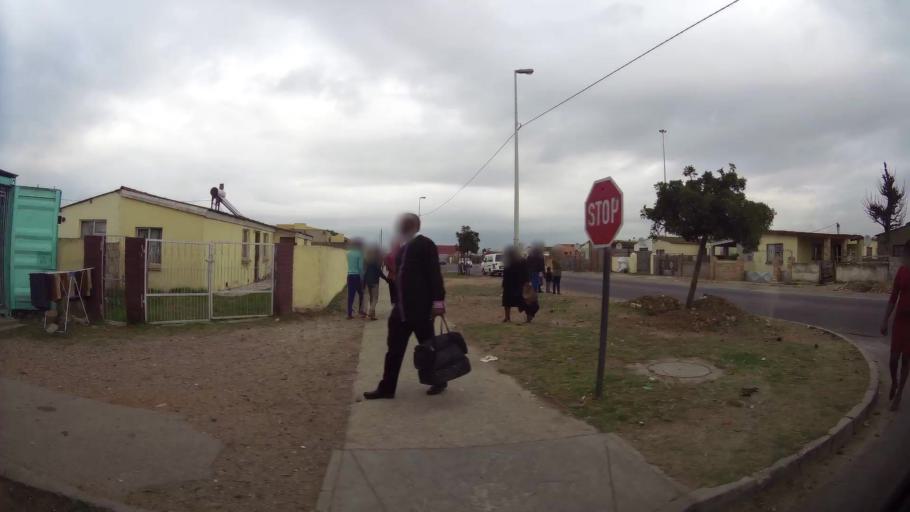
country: ZA
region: Eastern Cape
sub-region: Nelson Mandela Bay Metropolitan Municipality
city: Port Elizabeth
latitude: -33.8960
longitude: 25.6008
